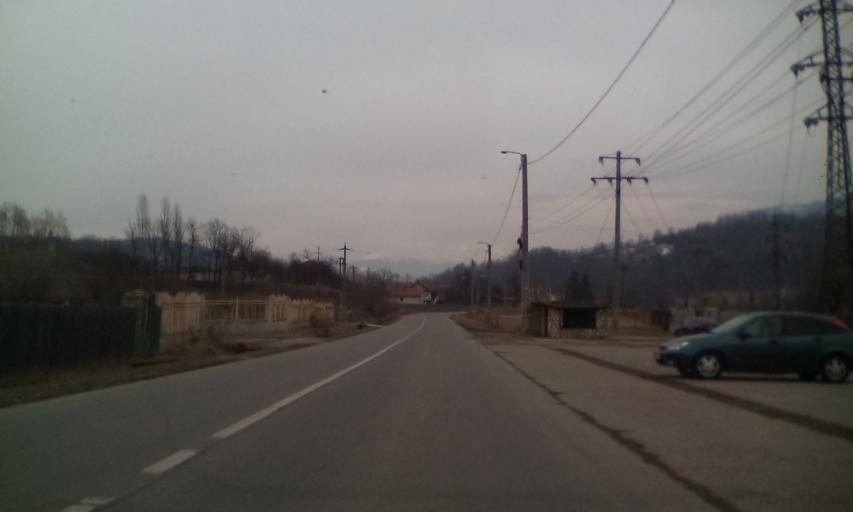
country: RO
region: Hunedoara
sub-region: Comuna Uricani
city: Uricani
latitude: 45.3380
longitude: 23.1455
